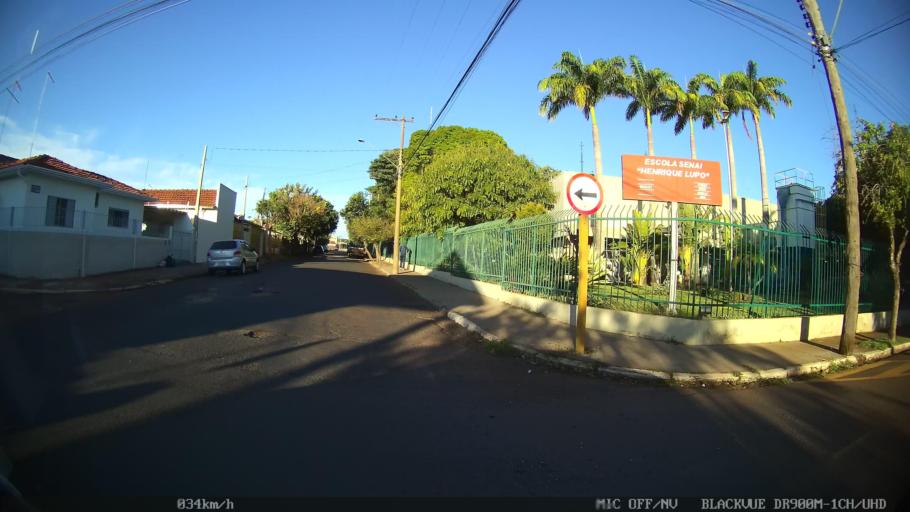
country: BR
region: Sao Paulo
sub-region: Araraquara
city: Araraquara
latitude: -21.8056
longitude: -48.1921
